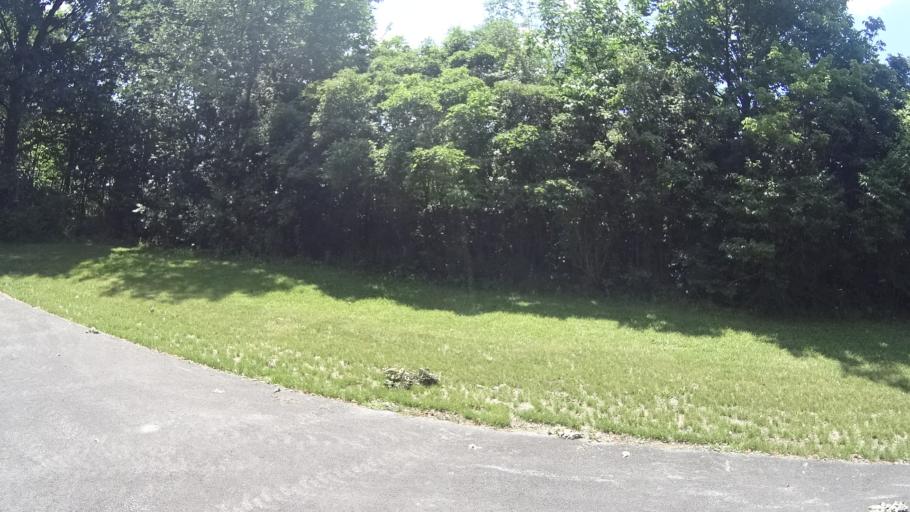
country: US
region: Ohio
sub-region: Erie County
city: Huron
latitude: 41.4062
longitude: -82.5968
